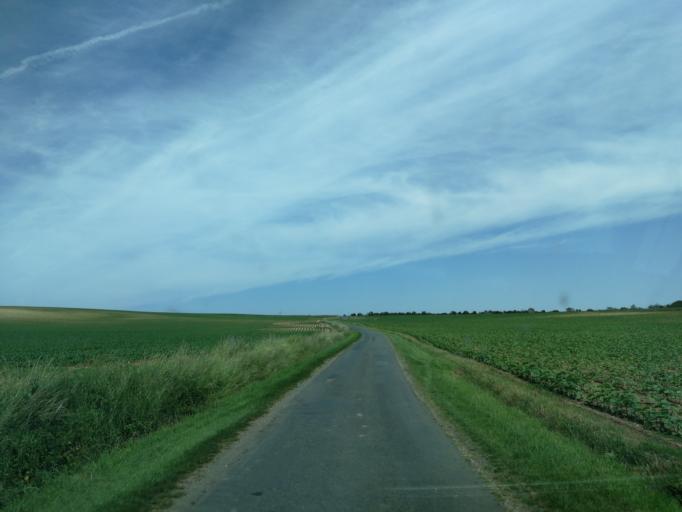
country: FR
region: Pays de la Loire
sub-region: Departement de la Vendee
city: Le Langon
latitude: 46.4218
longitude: -0.9001
